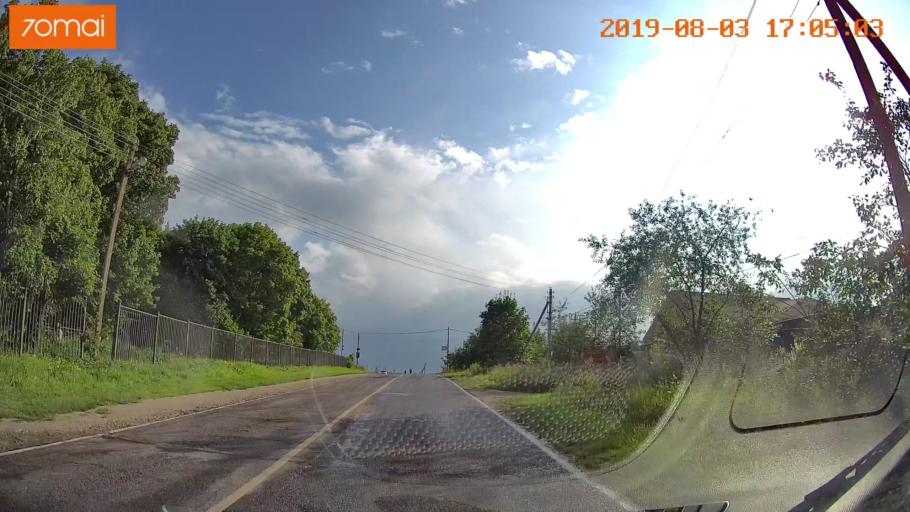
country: RU
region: Moskovskaya
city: Troitskoye
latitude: 55.3239
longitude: 38.5528
